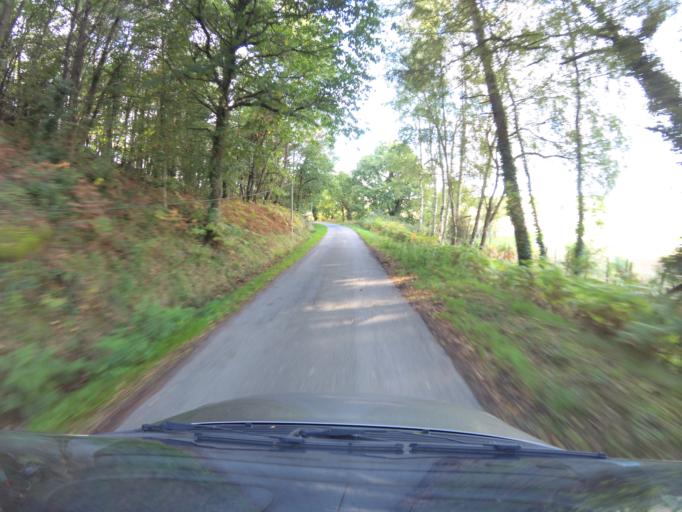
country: FR
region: Brittany
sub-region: Departement du Morbihan
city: Saint-Martin-sur-Oust
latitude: 47.7320
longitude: -2.2416
